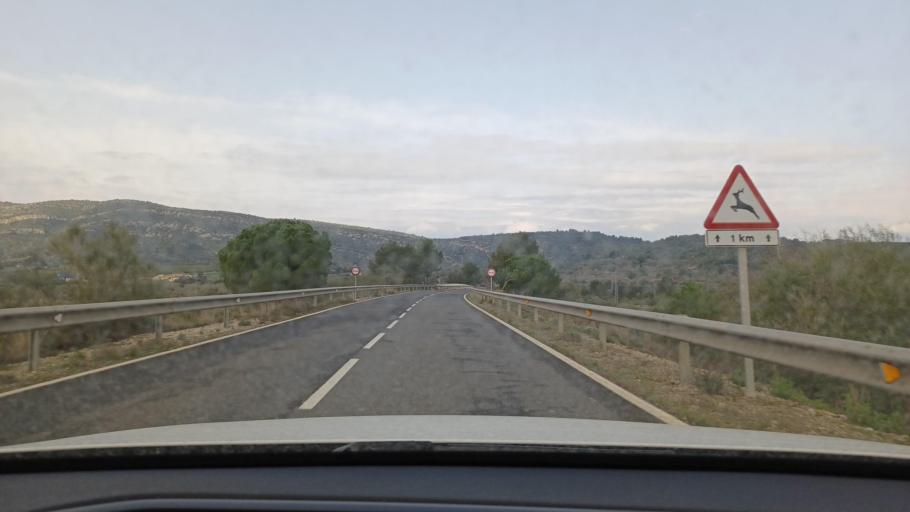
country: ES
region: Catalonia
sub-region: Provincia de Tarragona
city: Masdenverge
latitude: 40.6702
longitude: 0.5165
